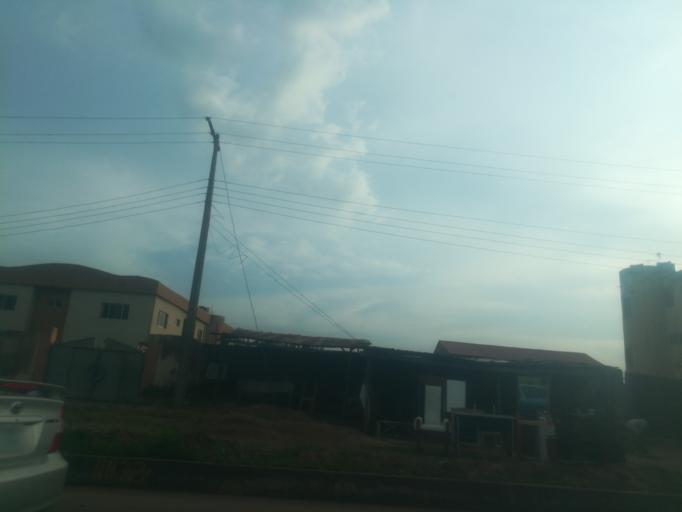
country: NG
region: Ogun
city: Abeokuta
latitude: 7.1649
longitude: 3.3088
